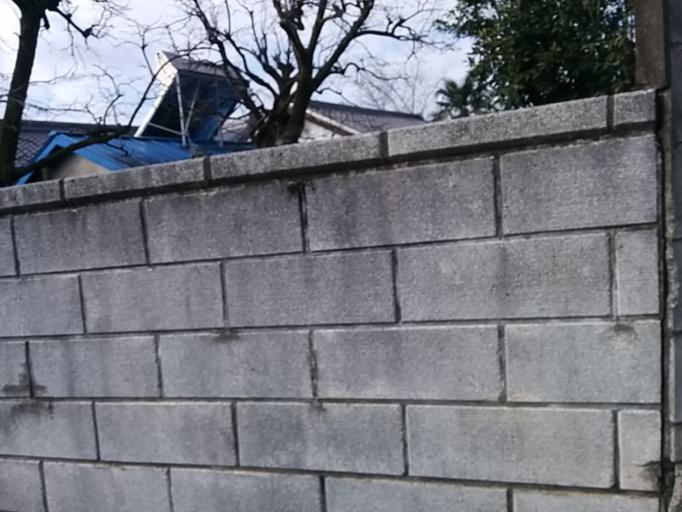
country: JP
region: Saitama
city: Kawagoe
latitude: 35.9094
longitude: 139.4928
